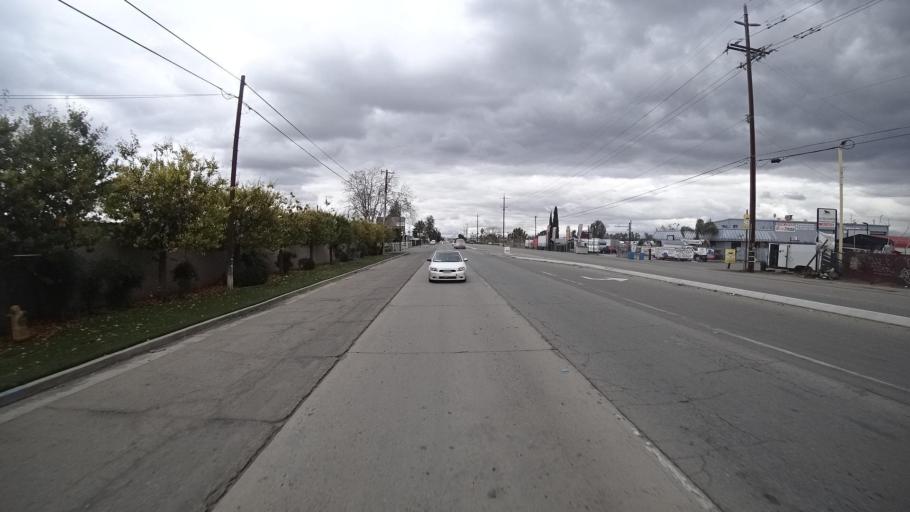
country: US
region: California
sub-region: Kern County
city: Greenfield
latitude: 35.3126
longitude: -119.0032
